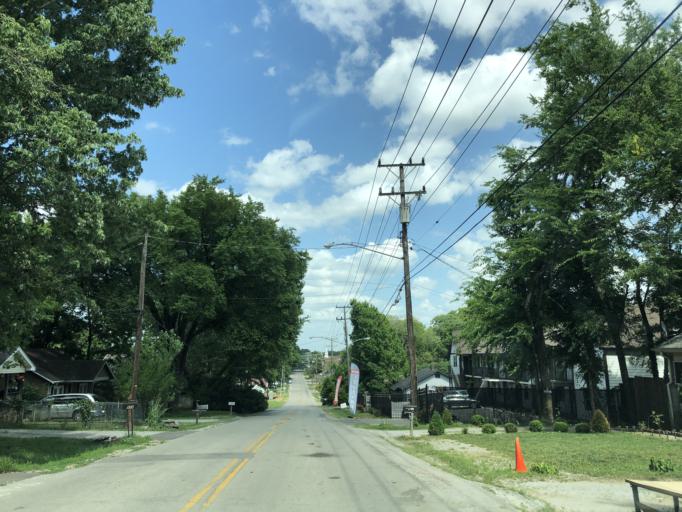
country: US
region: Tennessee
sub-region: Davidson County
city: Oak Hill
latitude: 36.0981
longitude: -86.7446
